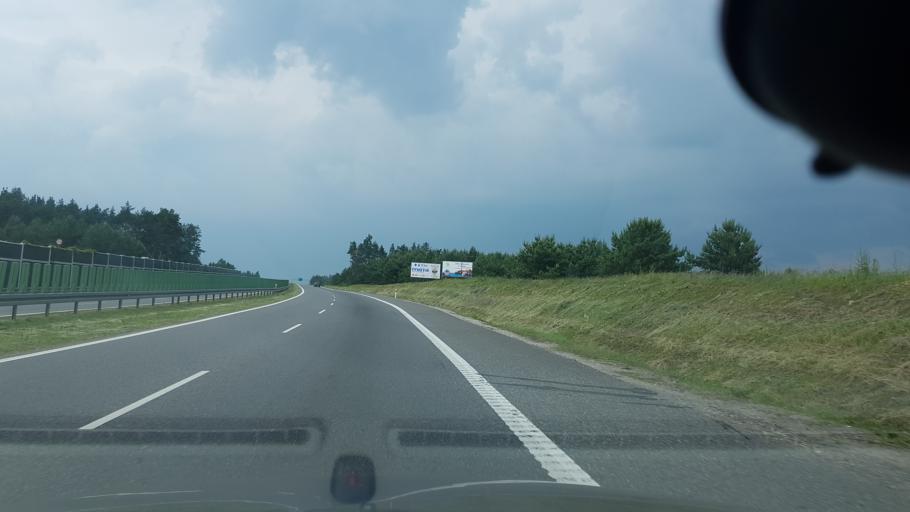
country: PL
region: Masovian Voivodeship
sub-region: Powiat legionowski
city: Serock
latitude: 52.5166
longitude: 21.0547
